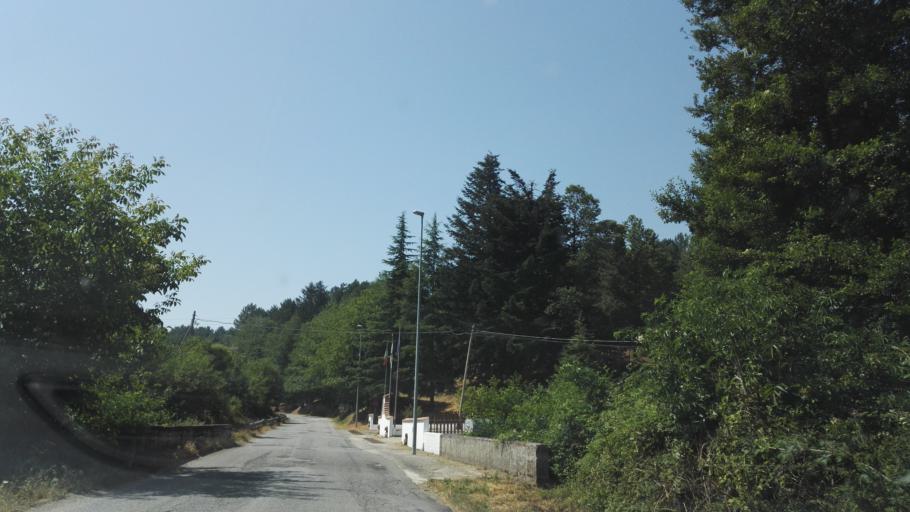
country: IT
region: Calabria
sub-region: Provincia di Vibo-Valentia
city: Mongiana
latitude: 38.5254
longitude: 16.3201
